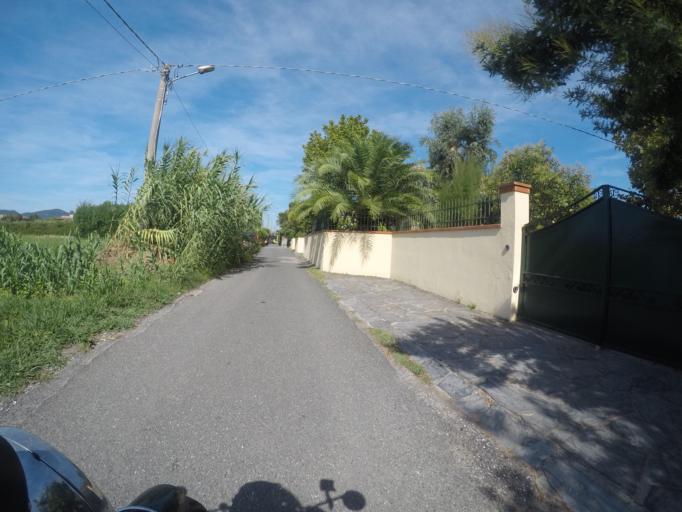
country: IT
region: Liguria
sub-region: Provincia di La Spezia
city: Casano-Dogana-Isola
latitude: 44.0605
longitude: 10.0328
